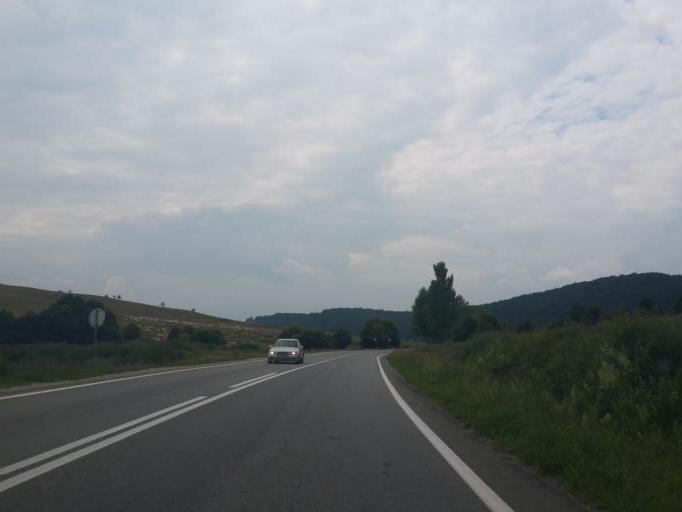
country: RO
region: Salaj
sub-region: Comuna Romanasi
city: Romanasi
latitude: 47.0584
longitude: 23.2170
